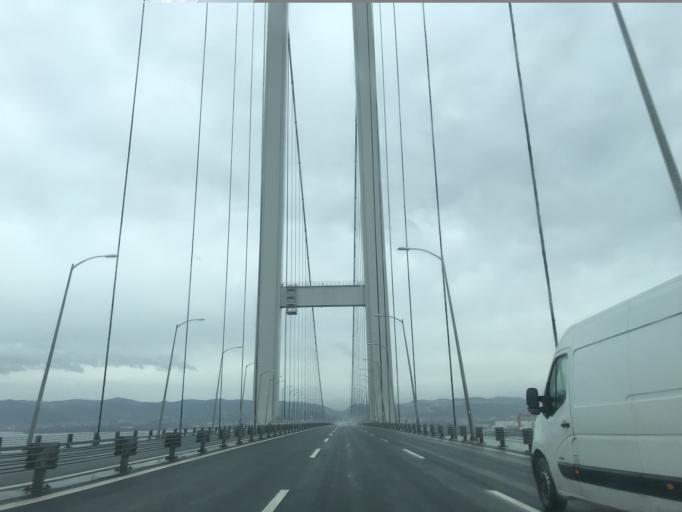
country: TR
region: Yalova
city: Altinova
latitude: 40.7498
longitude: 29.5150
